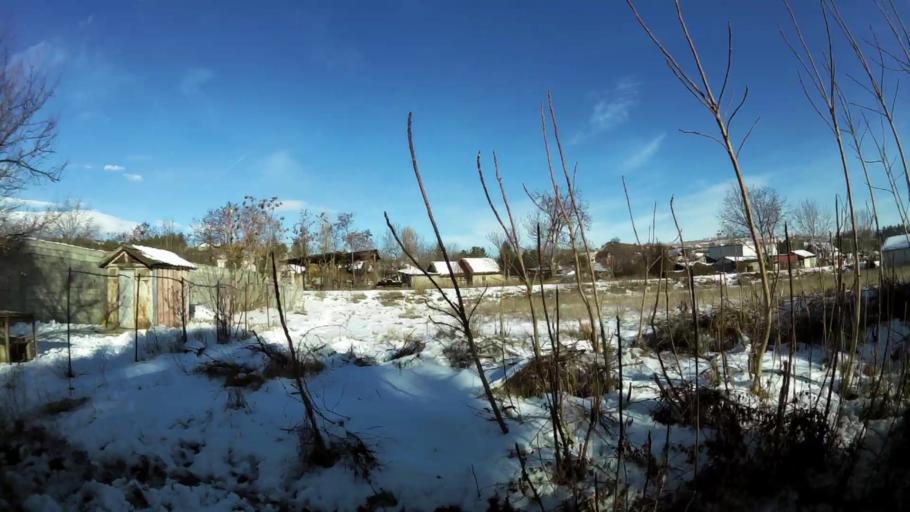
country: MK
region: Saraj
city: Saraj
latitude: 42.0096
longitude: 21.3346
